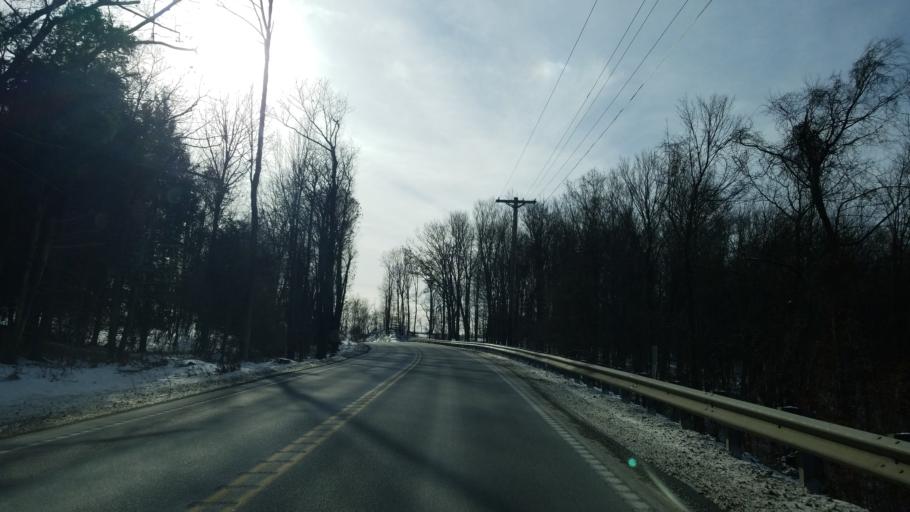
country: US
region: Pennsylvania
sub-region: Clearfield County
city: Treasure Lake
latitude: 41.1592
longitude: -78.5495
